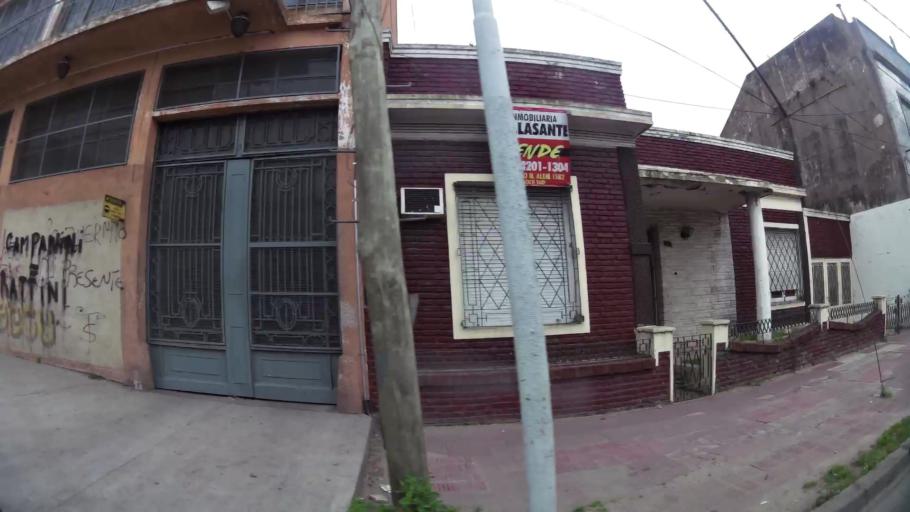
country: AR
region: Buenos Aires
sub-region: Partido de Avellaneda
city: Avellaneda
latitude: -34.6451
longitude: -58.3476
